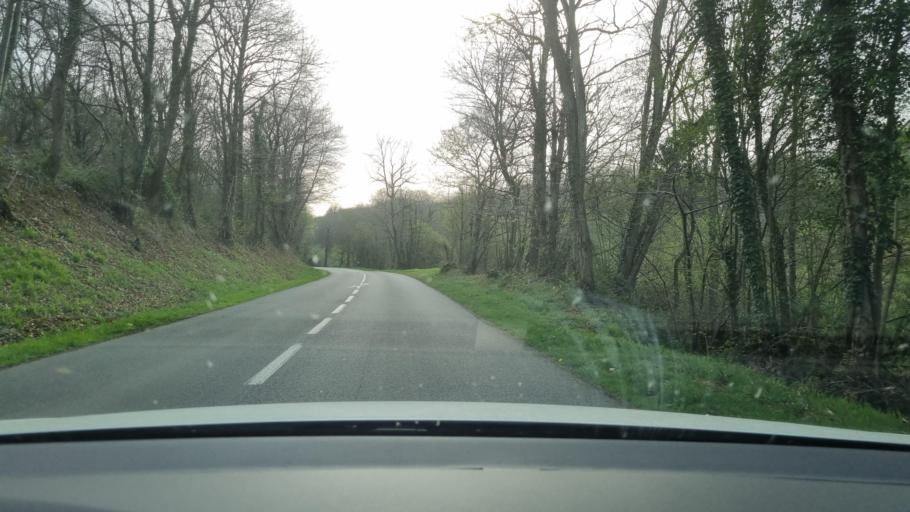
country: FR
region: Midi-Pyrenees
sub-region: Departement des Hautes-Pyrenees
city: Vic-en-Bigorre
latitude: 43.3801
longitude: -0.0173
